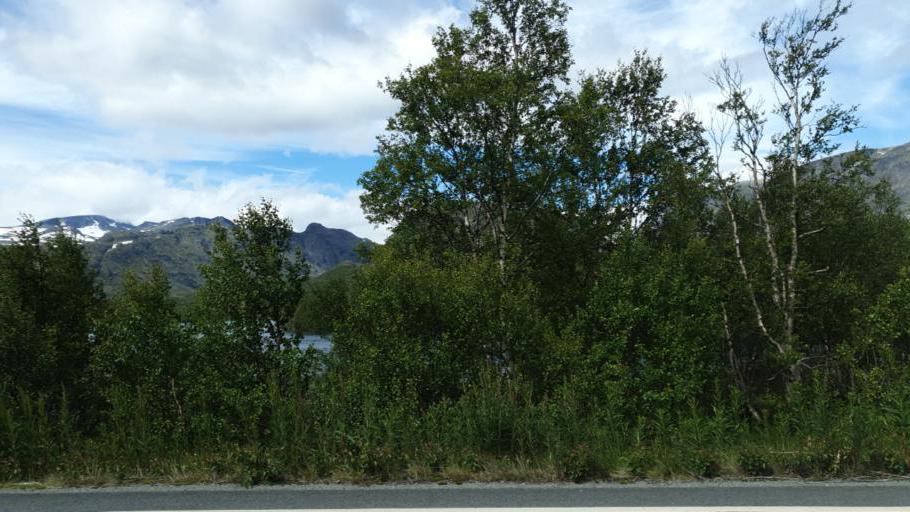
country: NO
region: Oppland
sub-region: Oystre Slidre
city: Heggenes
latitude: 61.4842
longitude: 8.8373
